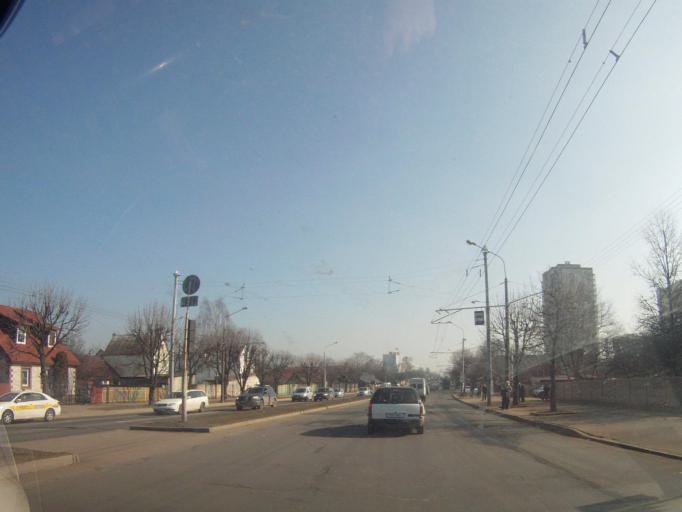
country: BY
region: Minsk
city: Minsk
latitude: 53.9321
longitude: 27.5474
